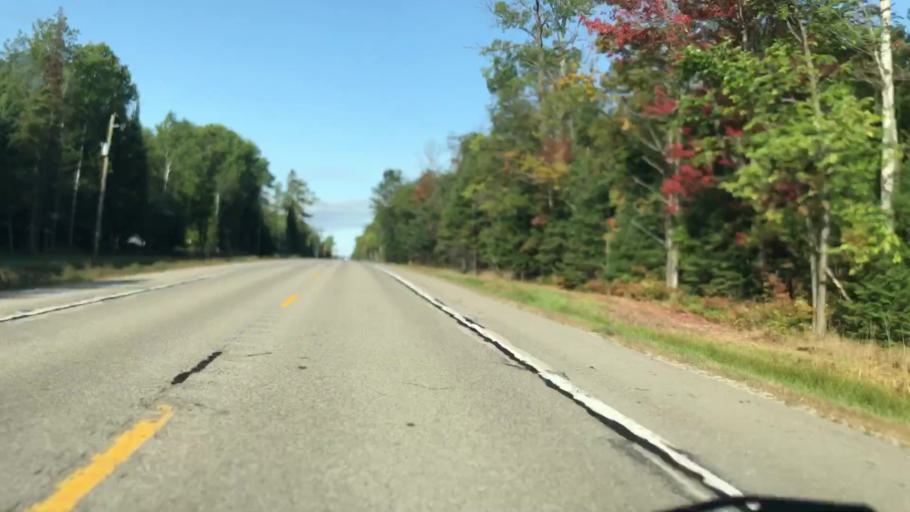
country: US
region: Michigan
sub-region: Luce County
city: Newberry
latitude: 46.3035
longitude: -85.3511
